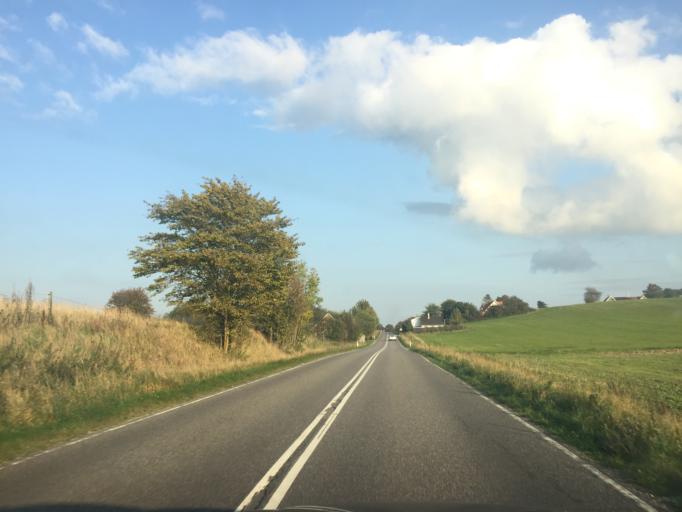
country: DK
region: Zealand
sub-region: Kalundborg Kommune
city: Hong
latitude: 55.5482
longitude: 11.3410
